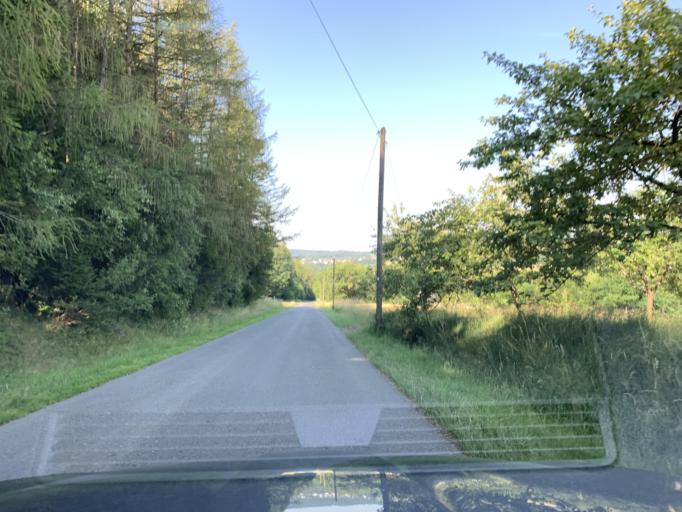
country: DE
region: Bavaria
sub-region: Upper Palatinate
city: Dieterskirchen
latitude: 49.4207
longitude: 12.4476
